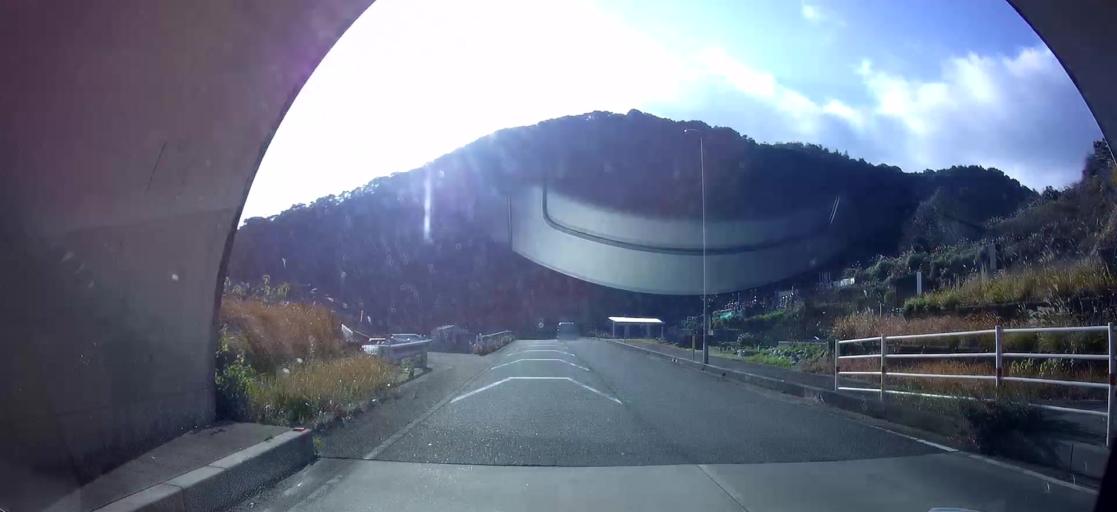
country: JP
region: Kumamoto
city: Minamata
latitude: 32.3923
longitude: 130.3866
